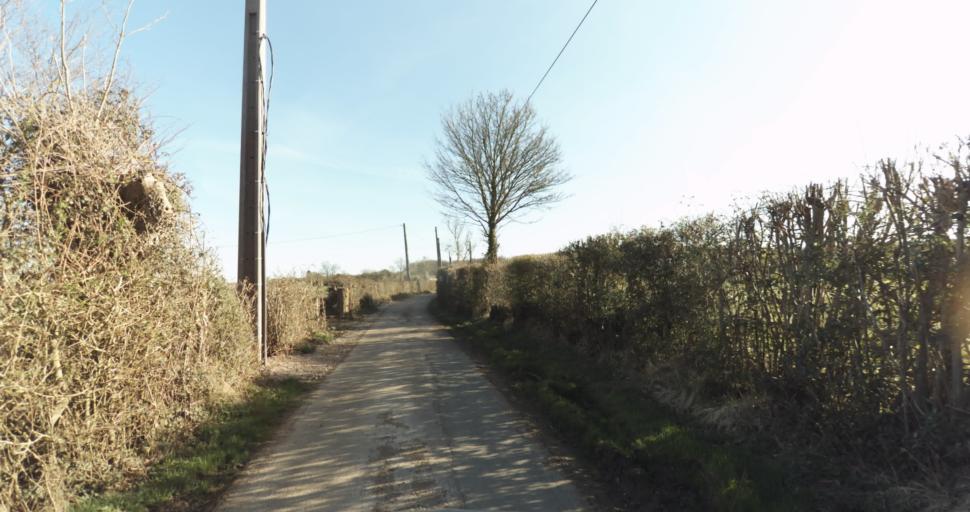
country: FR
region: Lower Normandy
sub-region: Departement du Calvados
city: Livarot
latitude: 48.9816
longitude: 0.0859
